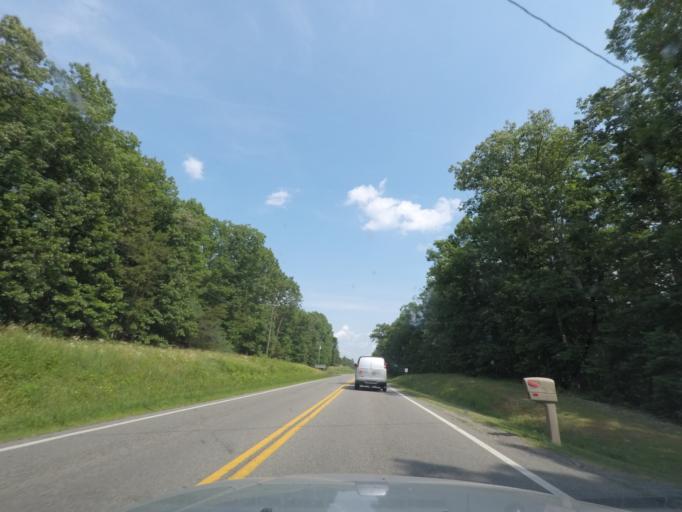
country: US
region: Virginia
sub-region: Fluvanna County
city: Palmyra
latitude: 37.8204
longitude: -78.2662
